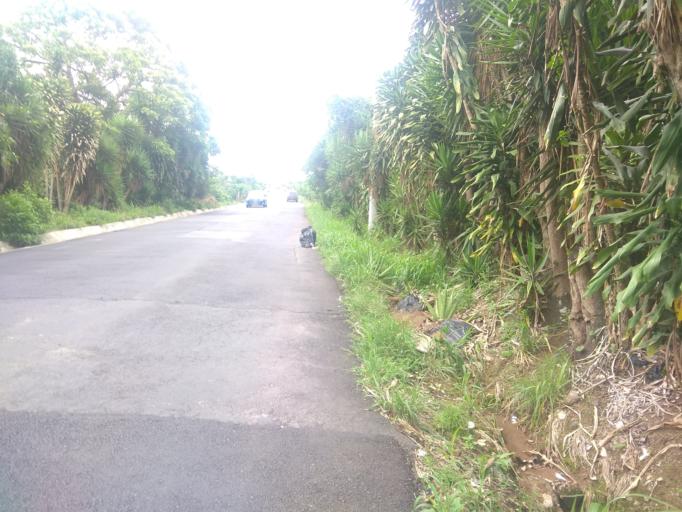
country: CR
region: Heredia
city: San Pablo
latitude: 9.9969
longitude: -84.1005
